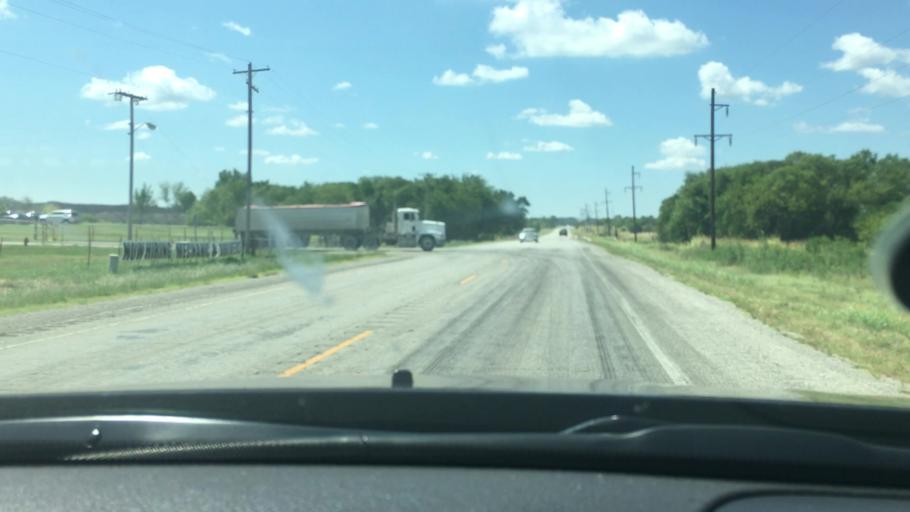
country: US
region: Oklahoma
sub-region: Carter County
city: Ardmore
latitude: 34.0794
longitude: -97.1429
